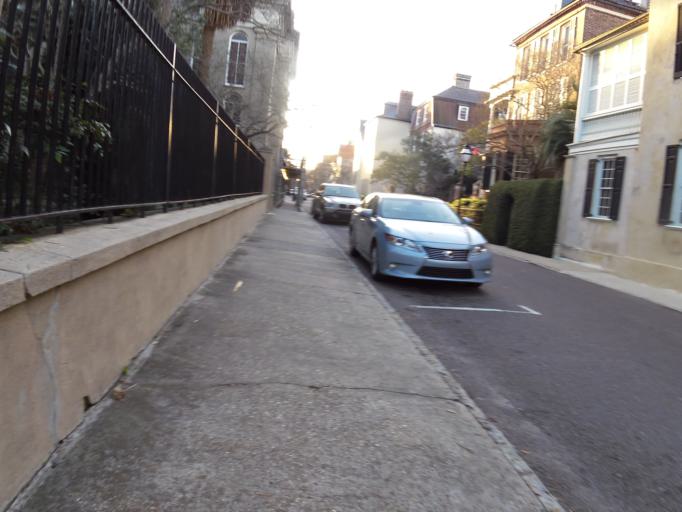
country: US
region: South Carolina
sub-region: Charleston County
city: Charleston
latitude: 32.7747
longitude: -79.9309
